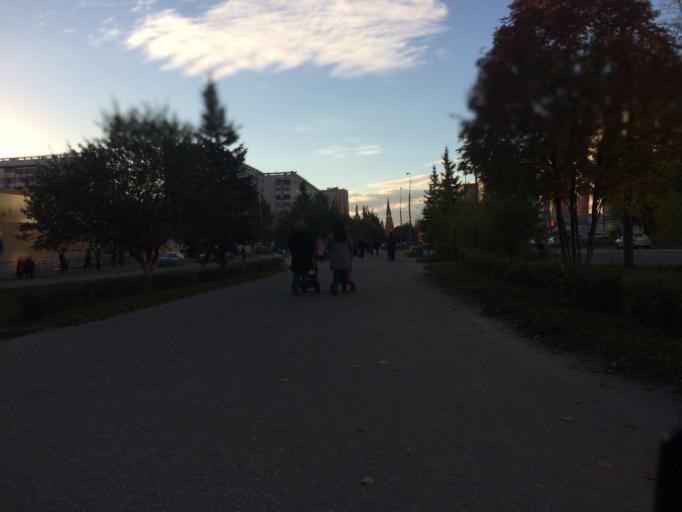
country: RU
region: Mariy-El
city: Yoshkar-Ola
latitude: 56.6302
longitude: 47.9198
